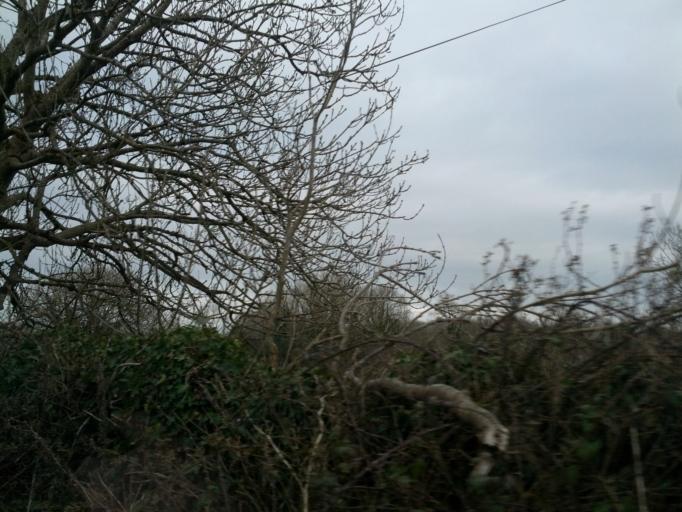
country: IE
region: Connaught
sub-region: County Galway
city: Oranmore
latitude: 53.1953
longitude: -8.9296
